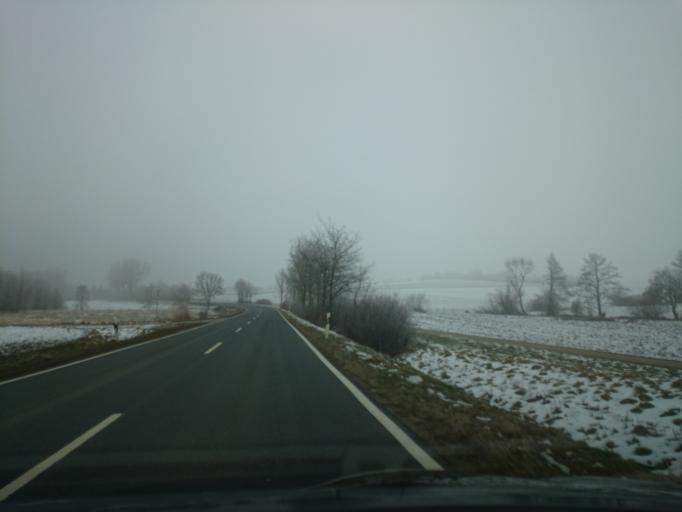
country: DE
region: Bavaria
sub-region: Regierungsbezirk Mittelfranken
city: Thalmassing
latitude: 49.1179
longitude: 11.2731
